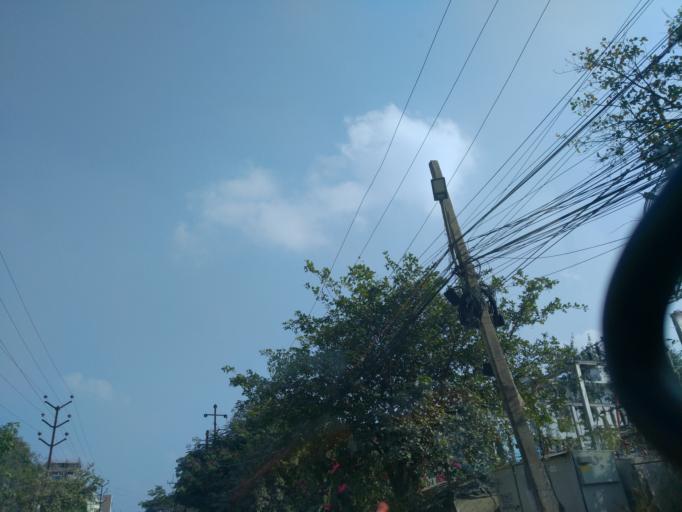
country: IN
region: Telangana
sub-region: Rangareddi
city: Kukatpalli
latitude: 17.4298
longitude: 78.4046
